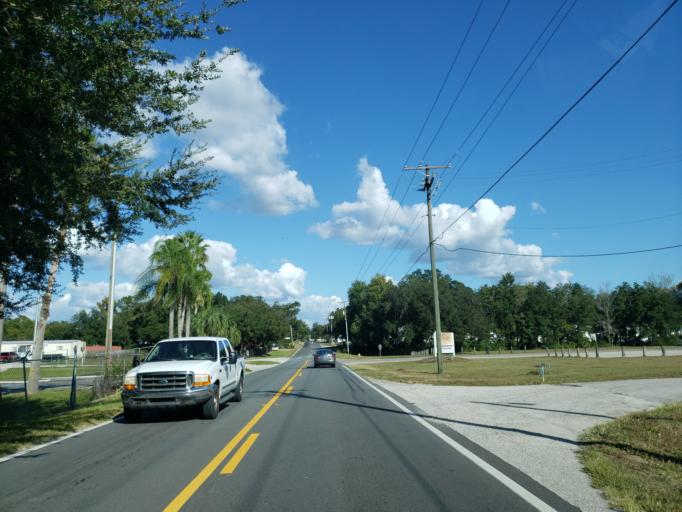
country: US
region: Florida
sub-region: Hillsborough County
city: Plant City
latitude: 28.0034
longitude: -82.1542
